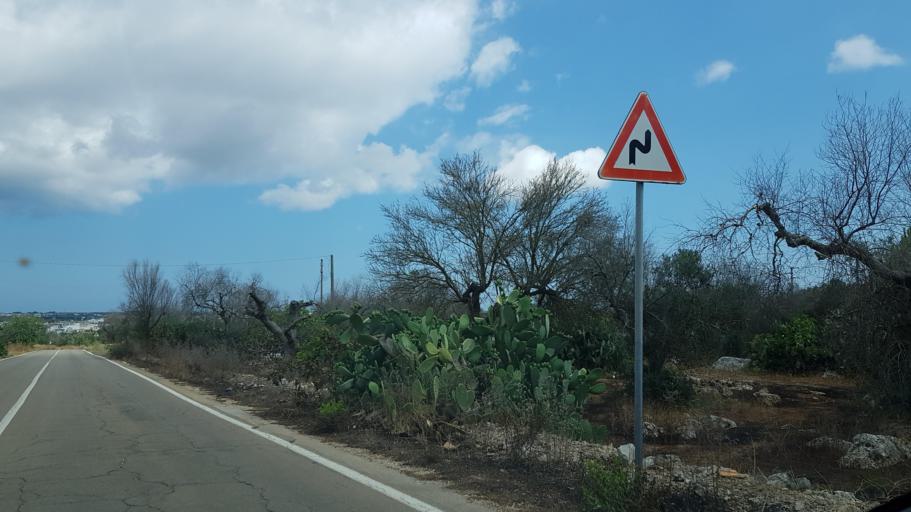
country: IT
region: Apulia
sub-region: Provincia di Lecce
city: Patu
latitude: 39.8454
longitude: 18.3259
